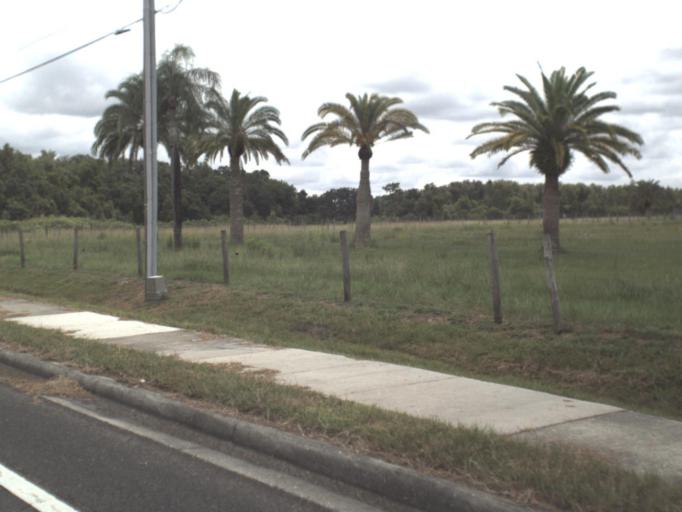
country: US
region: Florida
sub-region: Pasco County
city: Trinity
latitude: 28.2059
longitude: -82.6734
